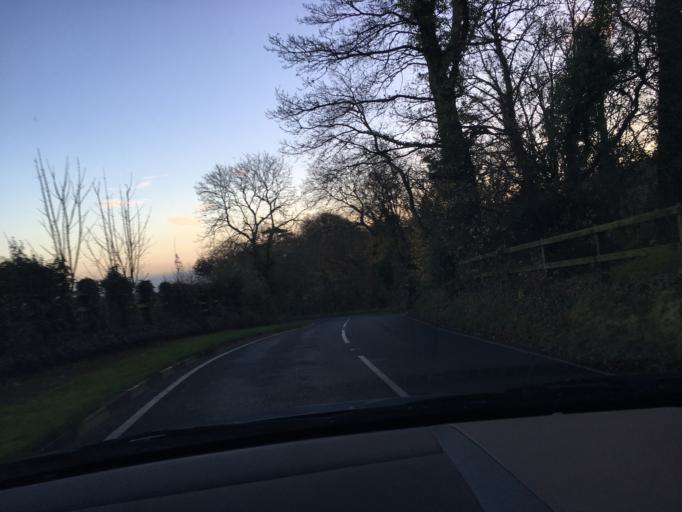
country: GB
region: England
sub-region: Isle of Wight
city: Shanklin
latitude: 50.6182
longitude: -1.1899
